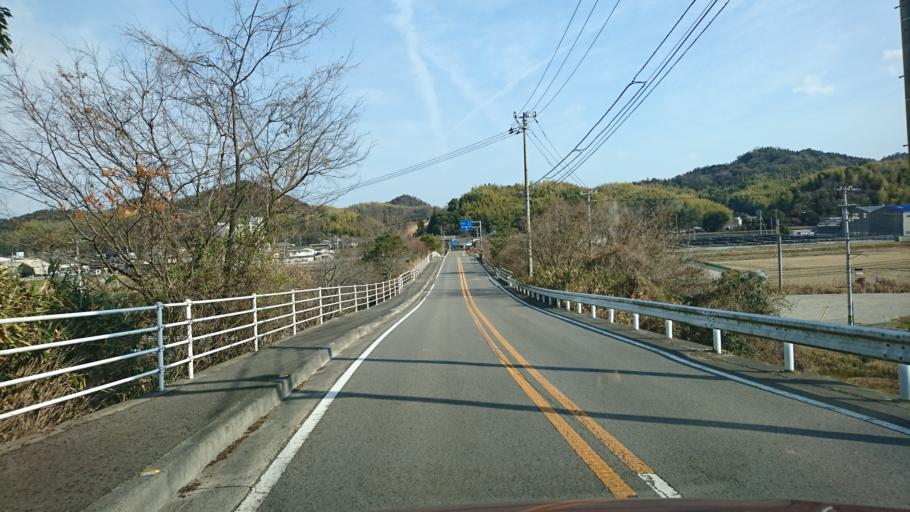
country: JP
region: Ehime
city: Saijo
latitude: 34.0060
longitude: 133.0351
